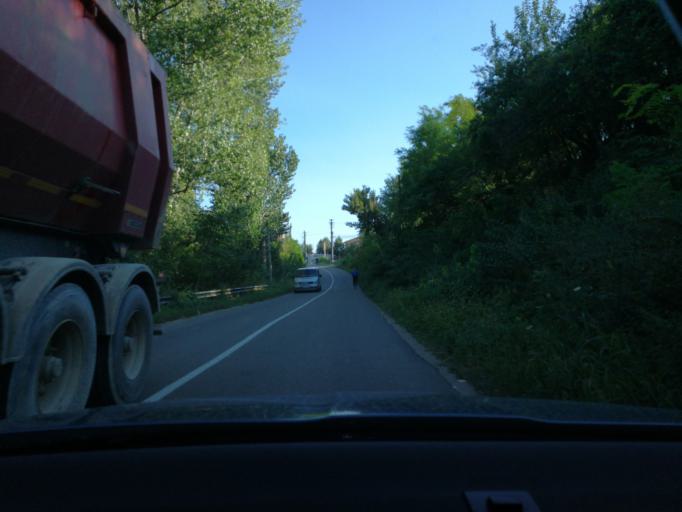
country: RO
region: Prahova
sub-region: Comuna Ceptura
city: Ceptura de Jos
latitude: 45.0220
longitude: 26.3256
